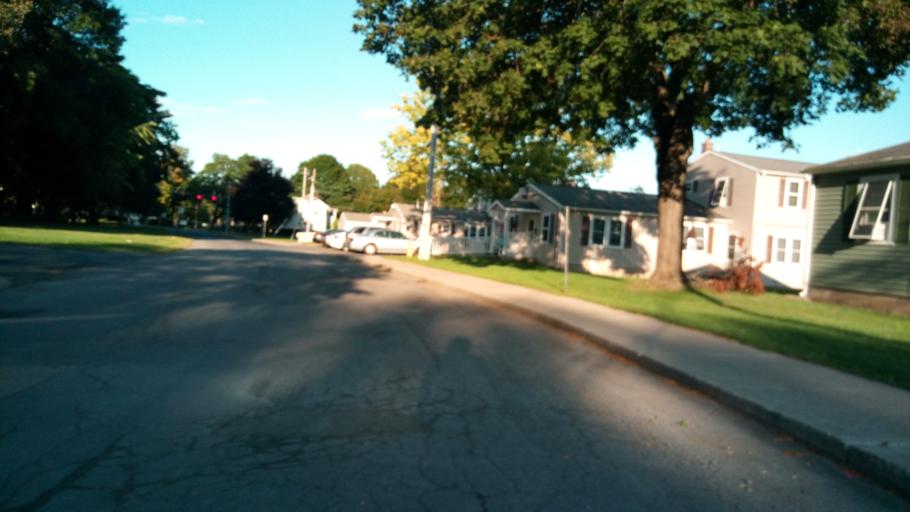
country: US
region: New York
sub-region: Chemung County
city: West Elmira
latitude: 42.0980
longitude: -76.8312
